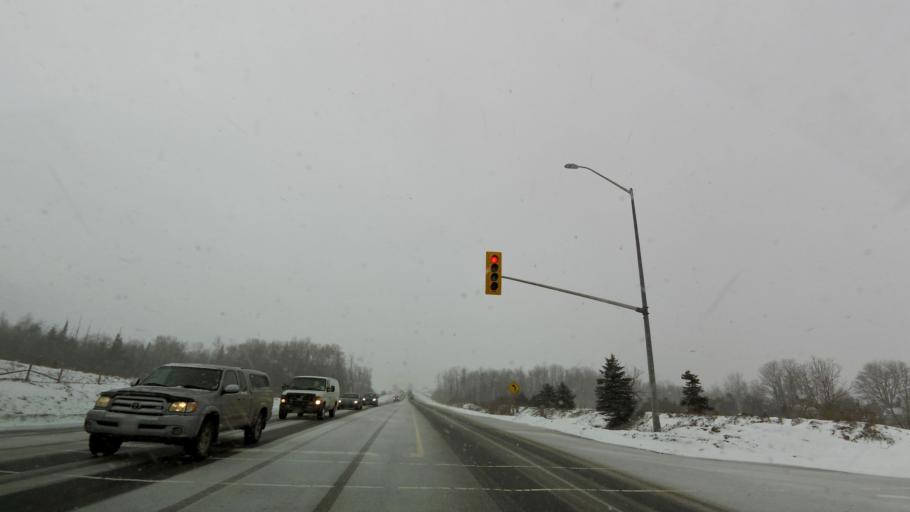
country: CA
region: Ontario
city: Orangeville
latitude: 43.9067
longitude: -80.0838
